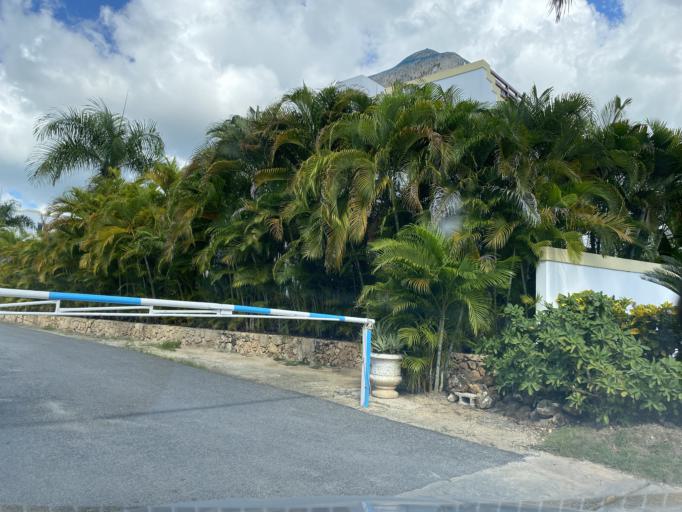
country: DO
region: La Romana
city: La Romana
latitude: 18.3497
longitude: -68.8239
